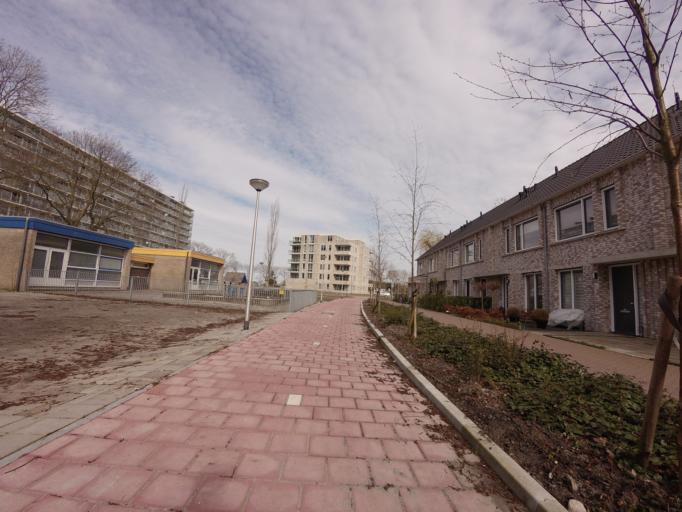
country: NL
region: North Holland
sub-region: Gemeente Uithoorn
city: Uithoorn
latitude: 52.2491
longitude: 4.8322
